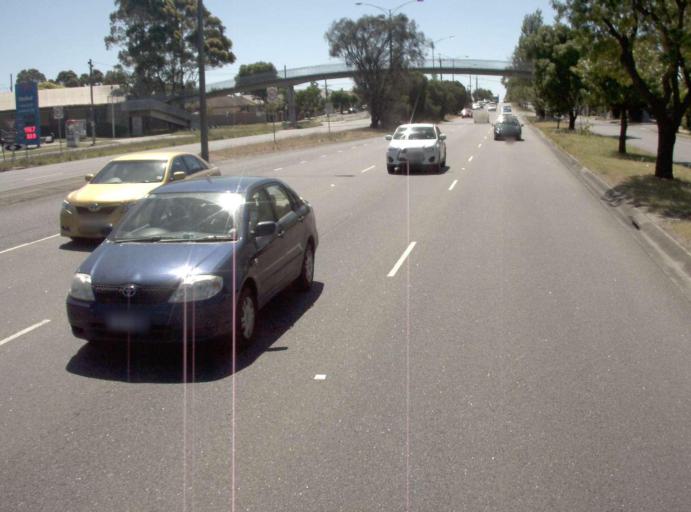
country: AU
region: Victoria
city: Clayton
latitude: -37.9067
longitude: 145.1153
